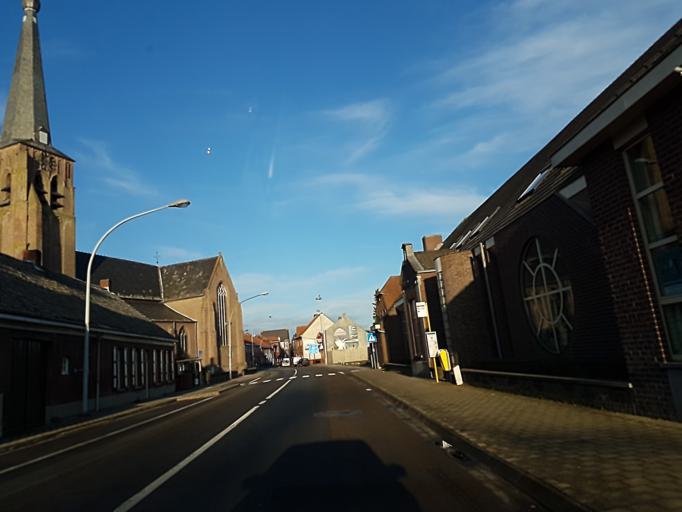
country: NL
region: North Brabant
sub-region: Gemeente Goirle
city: Goirle
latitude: 51.4454
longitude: 5.0385
